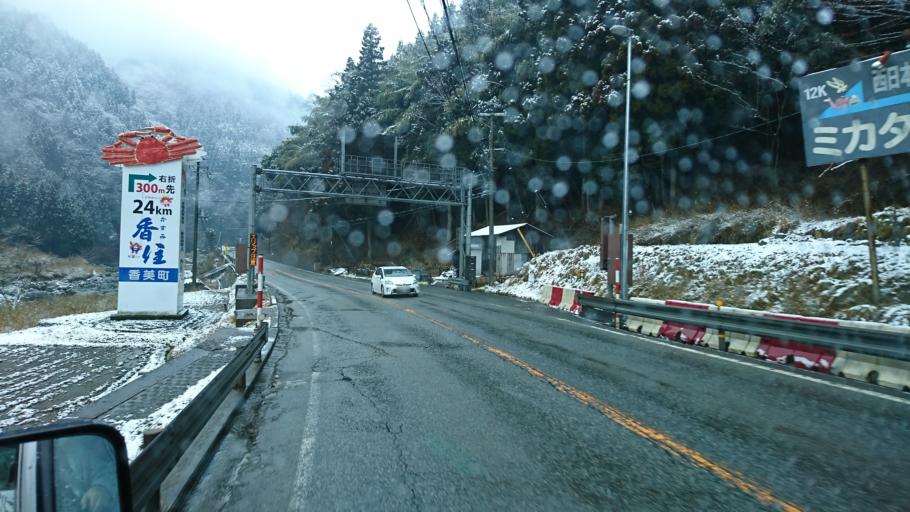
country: JP
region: Hyogo
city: Toyooka
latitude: 35.4892
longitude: 134.5736
